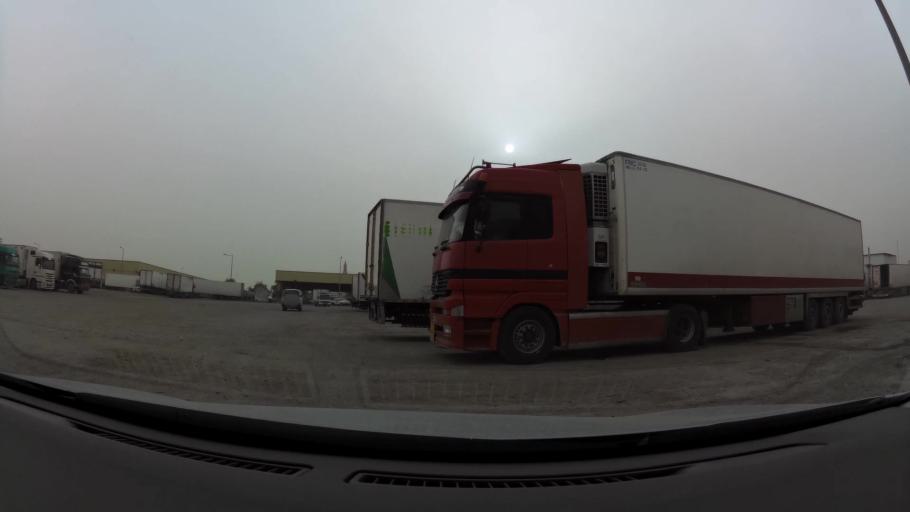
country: QA
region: Baladiyat ad Dawhah
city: Doha
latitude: 25.2475
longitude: 51.4783
